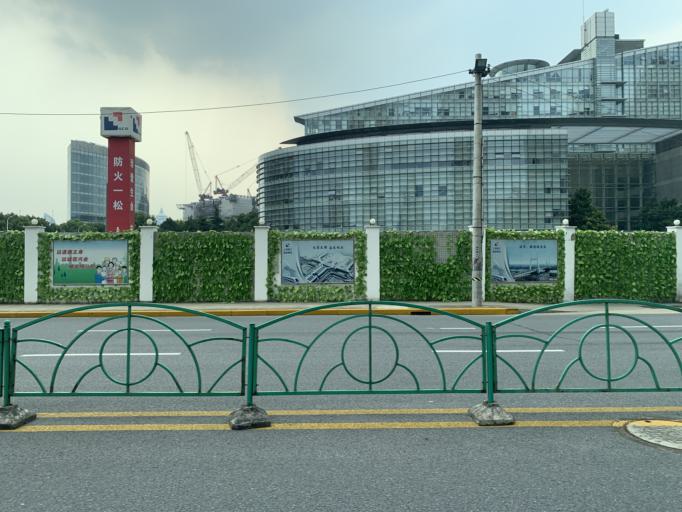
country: CN
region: Shanghai Shi
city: Huamu
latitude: 31.2211
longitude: 121.5393
